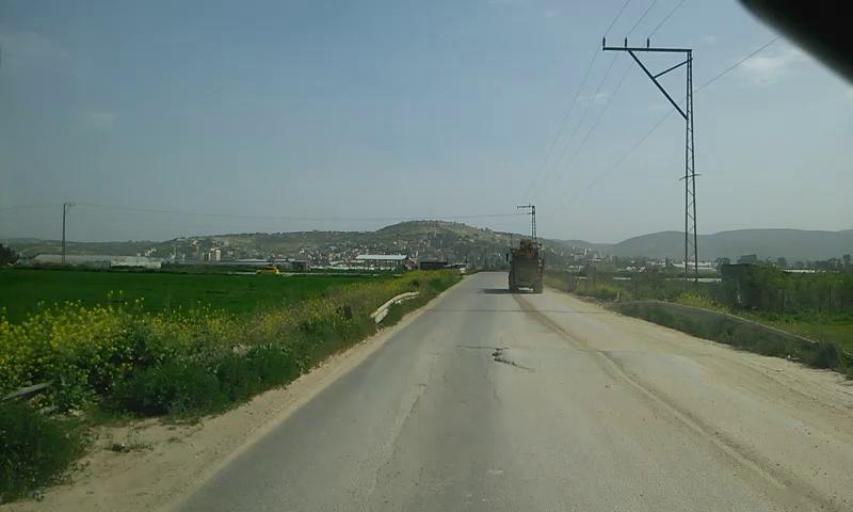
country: PS
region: West Bank
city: Ash Shuhada'
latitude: 32.4365
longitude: 35.2654
